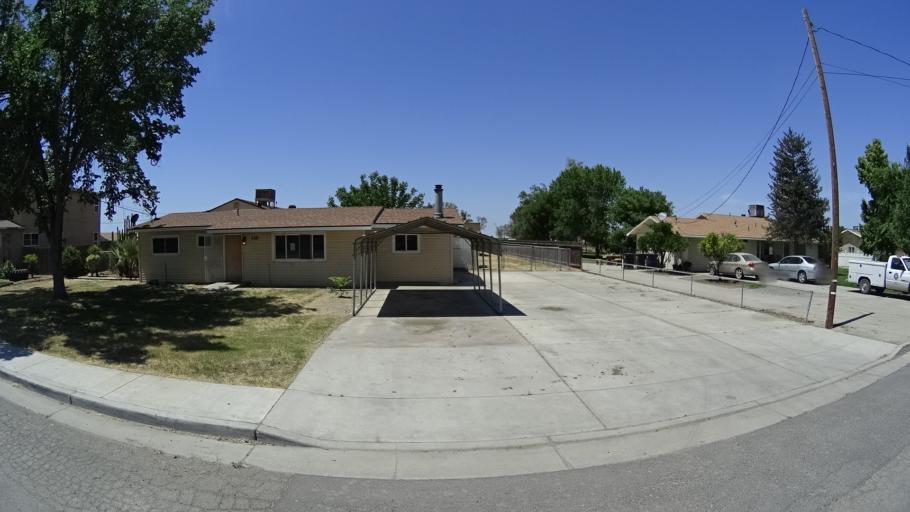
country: US
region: California
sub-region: Kings County
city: Corcoran
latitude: 36.1147
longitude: -119.5722
